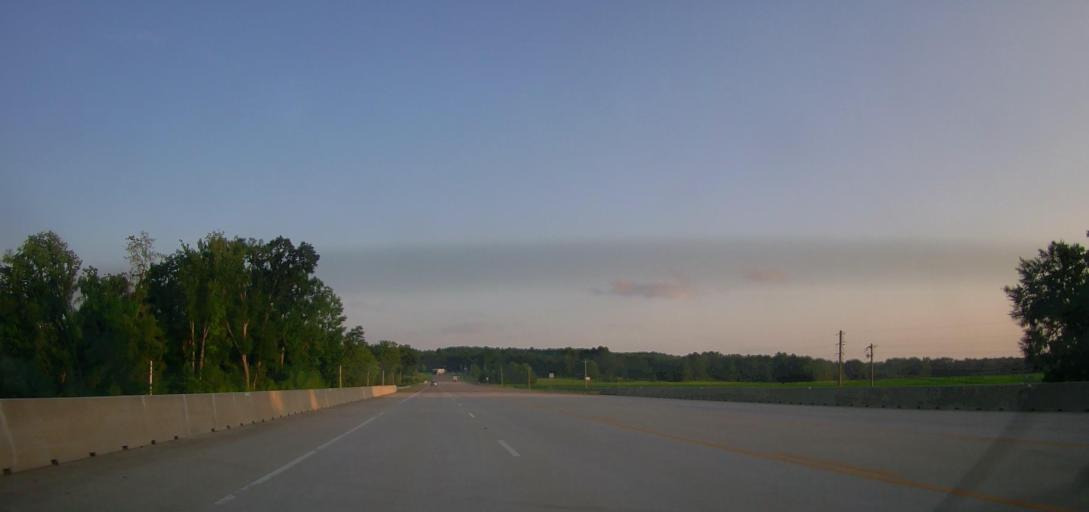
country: US
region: Alabama
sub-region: Marion County
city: Hamilton
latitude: 34.1063
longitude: -87.9891
